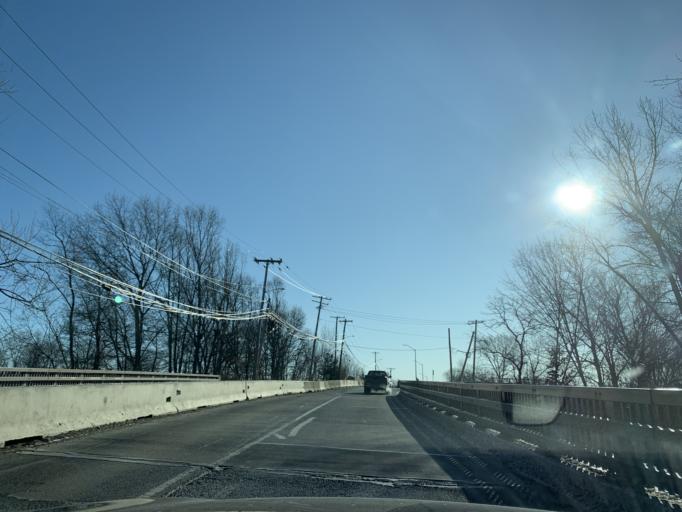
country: US
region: Massachusetts
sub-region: Norfolk County
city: Canton
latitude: 42.1971
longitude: -71.1552
